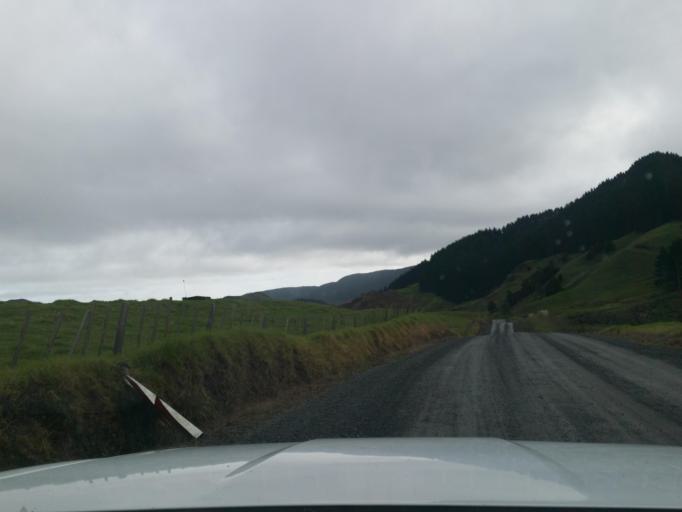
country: NZ
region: Northland
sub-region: Kaipara District
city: Dargaville
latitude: -35.8233
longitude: 173.8160
